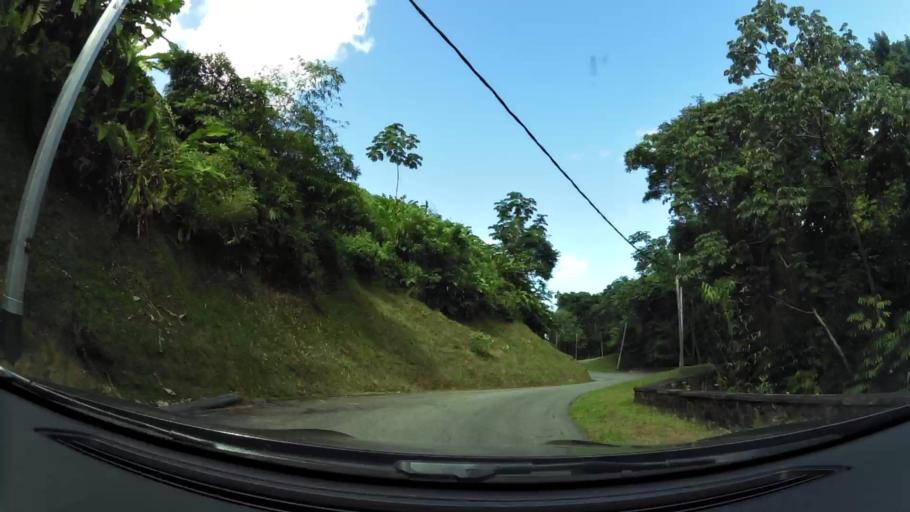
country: TT
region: Eastern Tobago
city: Roxborough
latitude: 11.3100
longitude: -60.6269
